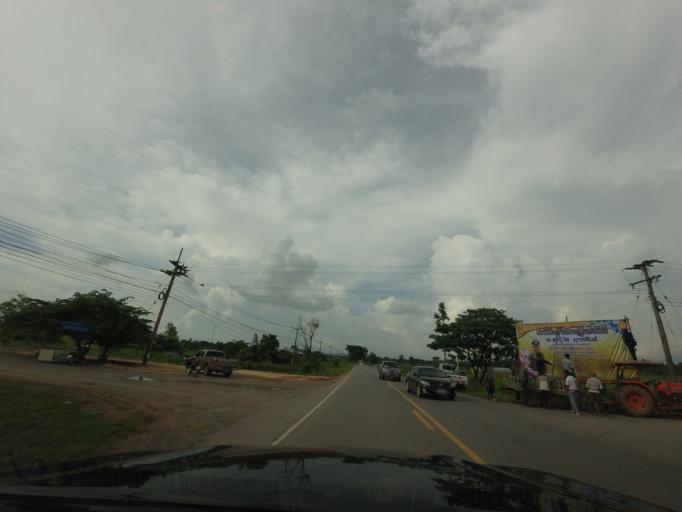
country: TH
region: Changwat Nong Bua Lamphu
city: Suwannakhuha
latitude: 17.4210
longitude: 102.3362
